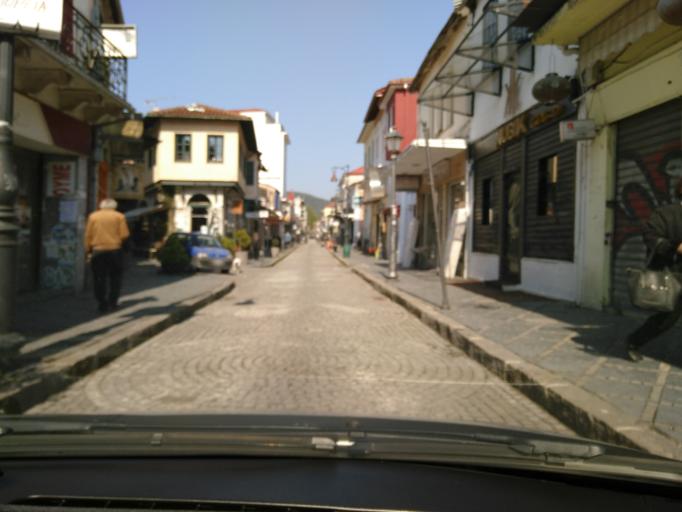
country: GR
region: Epirus
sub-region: Nomos Ioanninon
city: Ioannina
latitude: 39.6693
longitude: 20.8548
